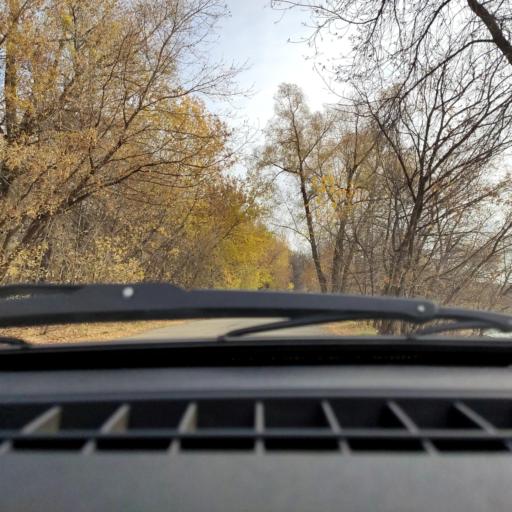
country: RU
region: Bashkortostan
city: Ufa
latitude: 54.7847
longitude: 56.1660
